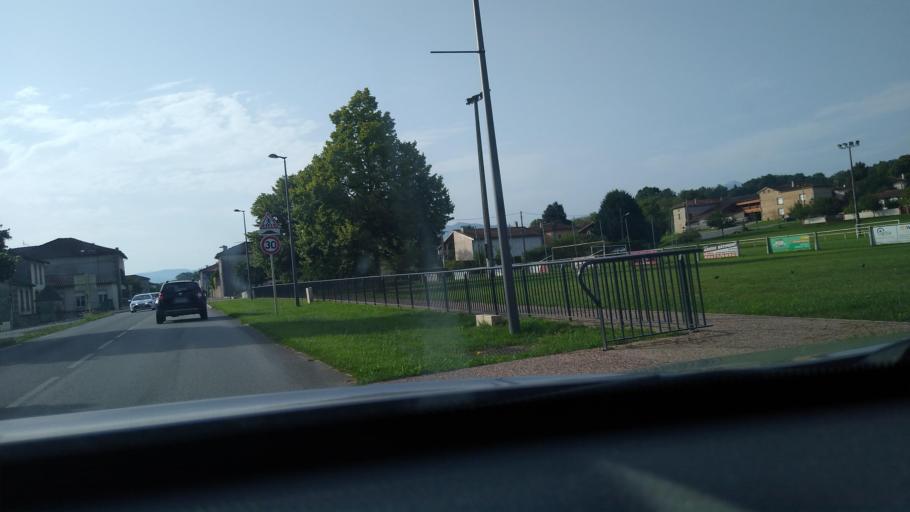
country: FR
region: Midi-Pyrenees
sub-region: Departement de l'Ariege
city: Saint-Lizier
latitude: 43.0295
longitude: 1.0853
